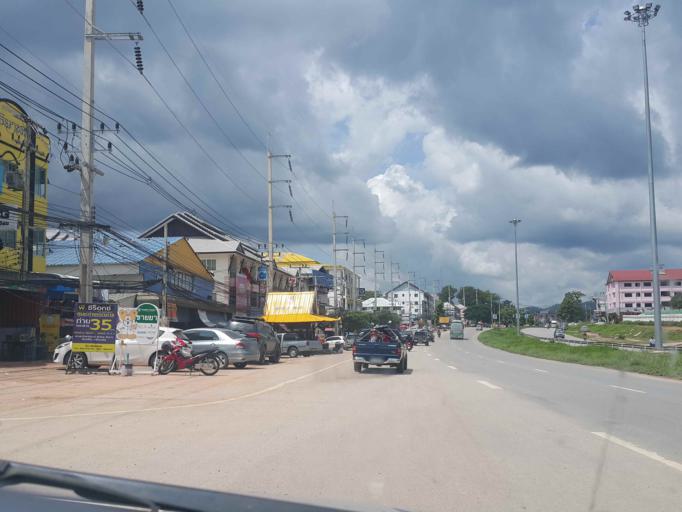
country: TH
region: Phayao
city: Dok Kham Tai
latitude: 19.0306
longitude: 99.9265
